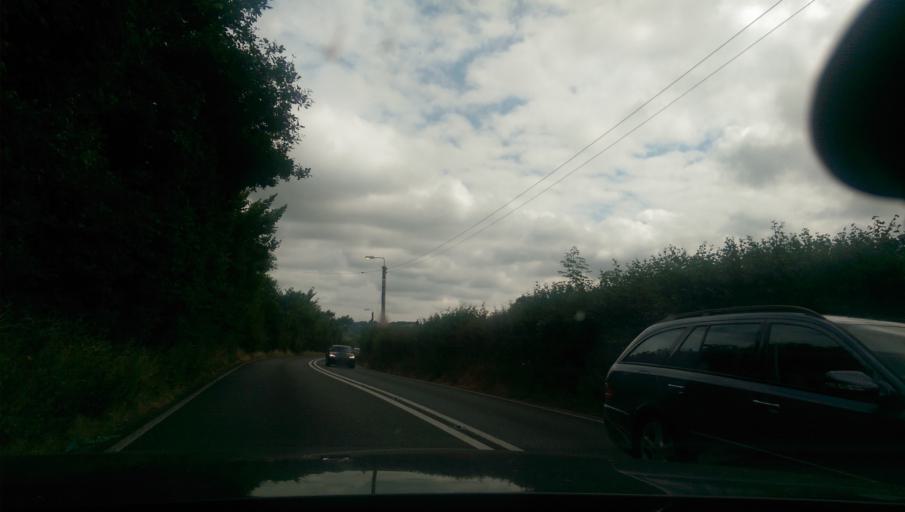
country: GB
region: England
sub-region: Devon
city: Honiton
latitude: 50.8149
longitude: -3.1660
